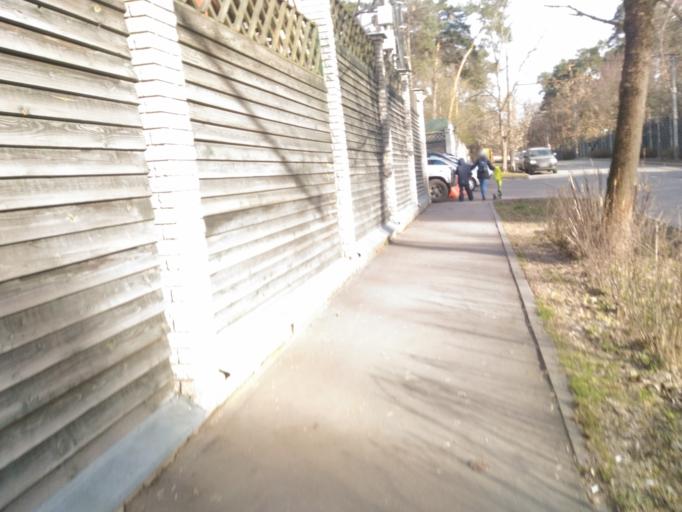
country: RU
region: Moscow
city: Strogino
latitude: 55.7875
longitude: 37.4180
